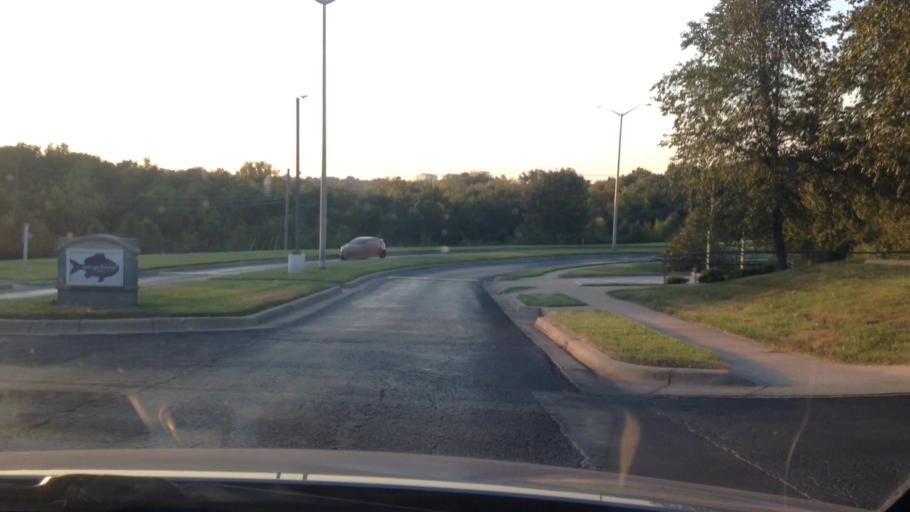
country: US
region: Missouri
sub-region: Jackson County
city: Grandview
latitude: 38.9224
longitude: -94.5587
